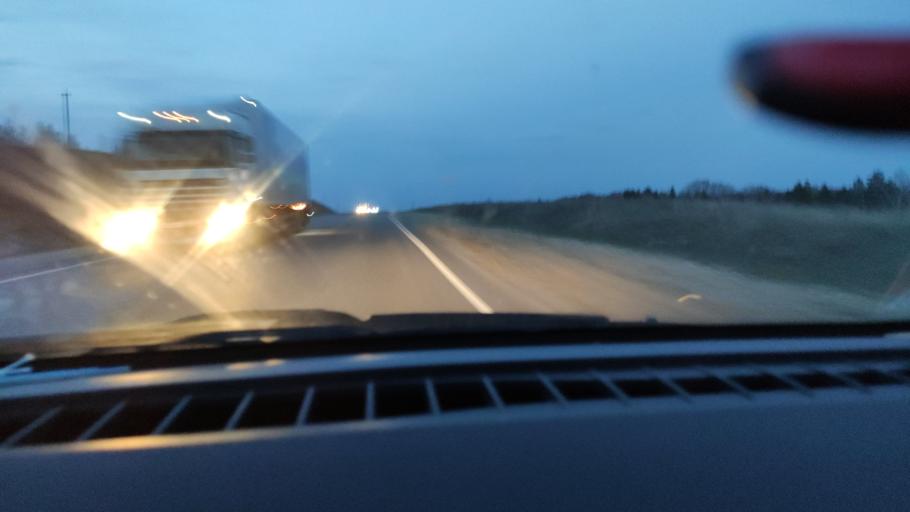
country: RU
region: Saratov
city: Sinodskoye
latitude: 52.0726
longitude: 46.7809
